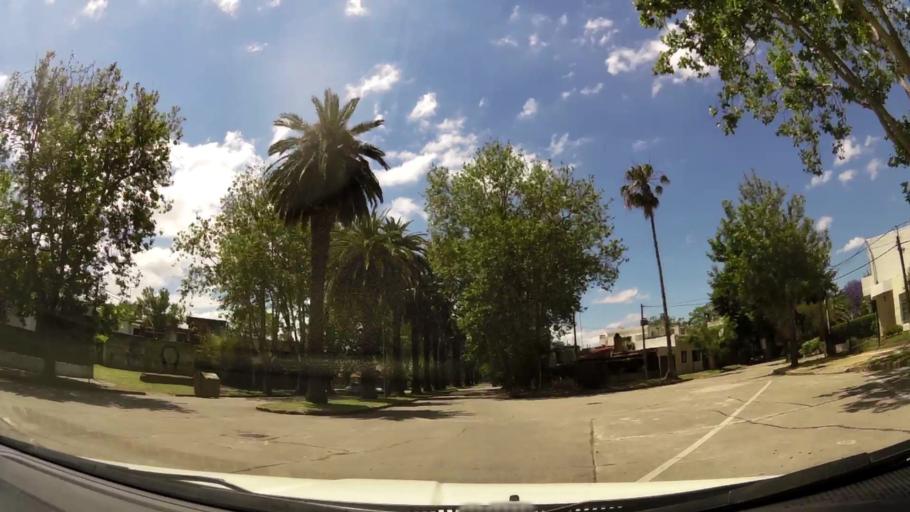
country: UY
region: Montevideo
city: Montevideo
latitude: -34.8679
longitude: -56.2002
